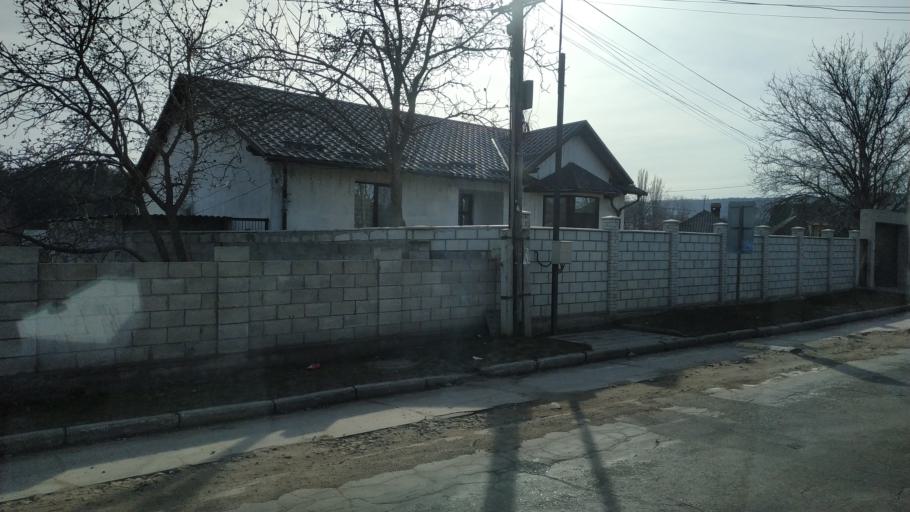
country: MD
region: Chisinau
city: Vatra
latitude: 47.0727
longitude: 28.6914
